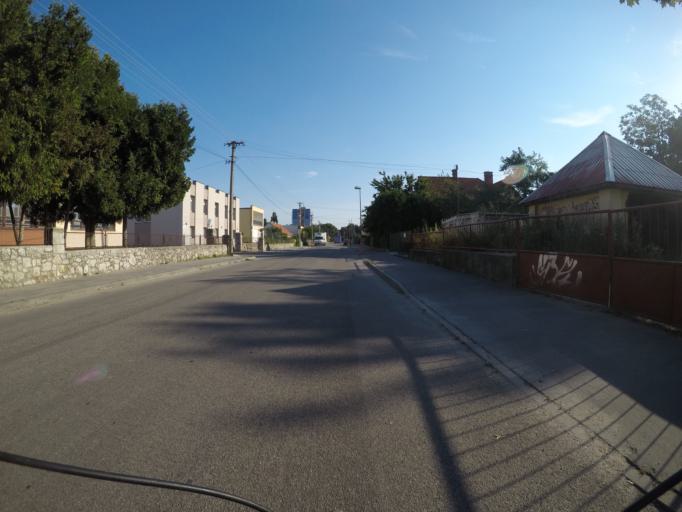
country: SK
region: Trenciansky
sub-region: Okres Nove Mesto nad Vahom
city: Nove Mesto nad Vahom
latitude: 48.7580
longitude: 17.8237
